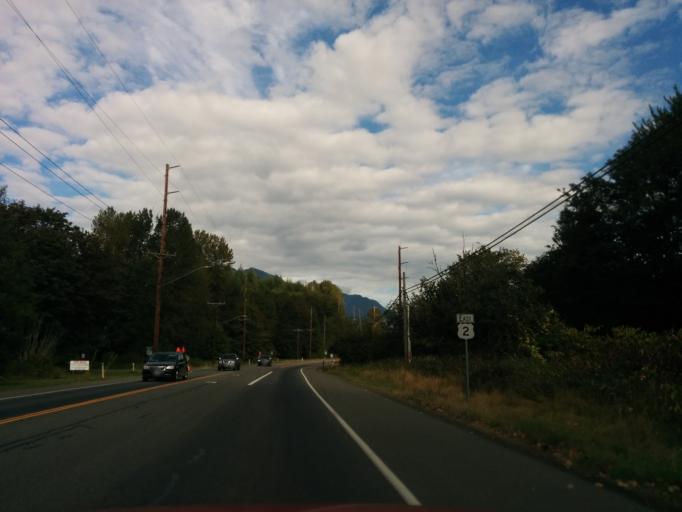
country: US
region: Washington
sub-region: Snohomish County
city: Gold Bar
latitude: 47.8671
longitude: -121.7360
